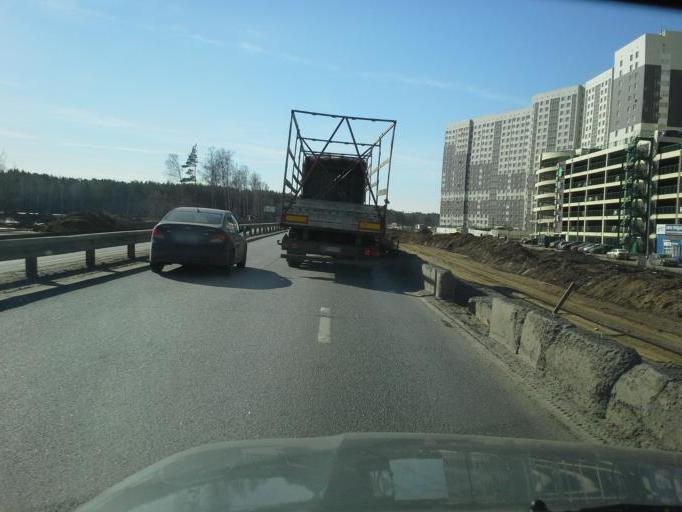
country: RU
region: Moskovskaya
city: Odintsovo
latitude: 55.6623
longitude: 37.3031
